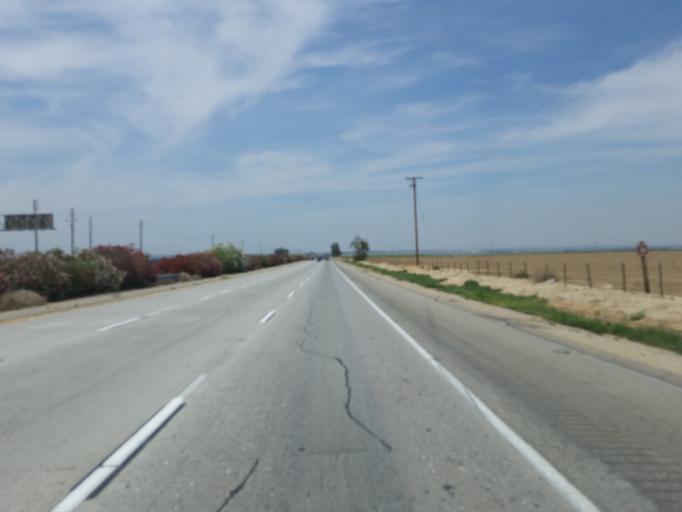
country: US
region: California
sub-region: Kern County
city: Weedpatch
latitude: 35.0975
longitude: -118.9802
